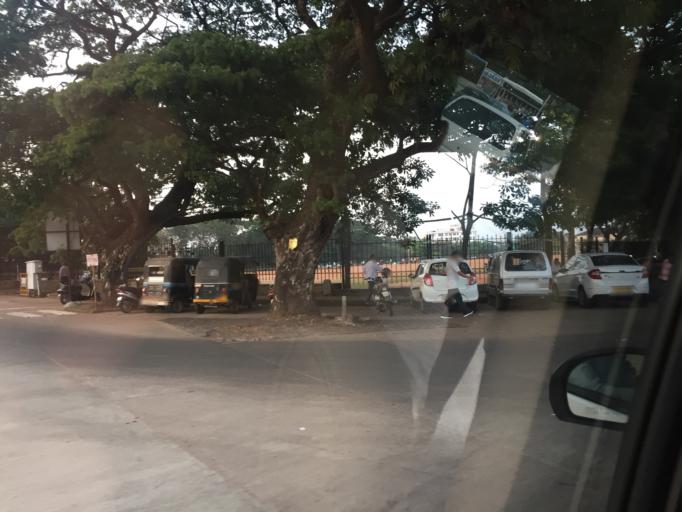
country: IN
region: Karnataka
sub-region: Dakshina Kannada
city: Ullal
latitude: 12.8609
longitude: 74.8389
